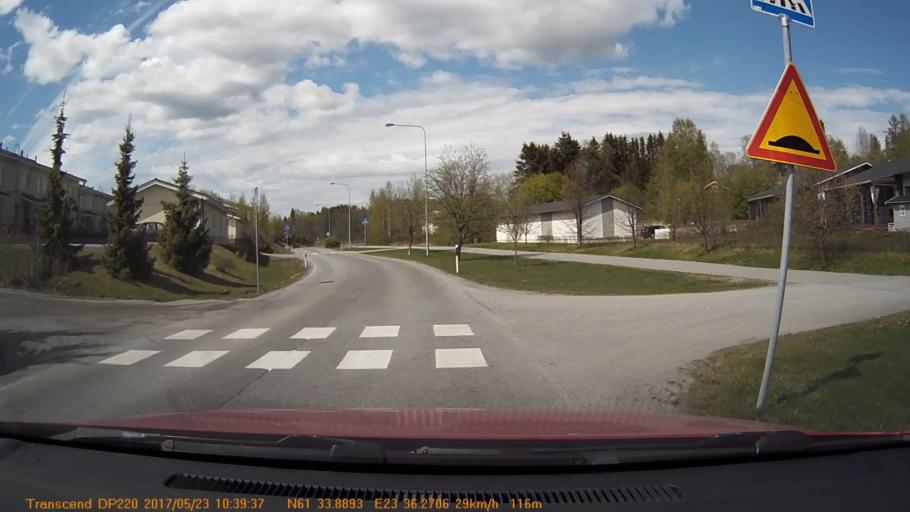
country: FI
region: Pirkanmaa
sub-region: Tampere
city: Yloejaervi
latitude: 61.5648
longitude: 23.6046
